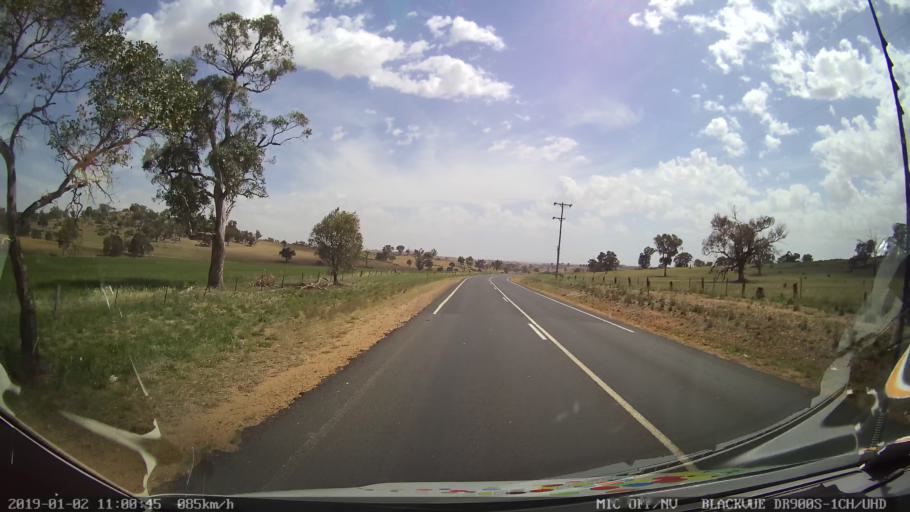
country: AU
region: New South Wales
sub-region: Cootamundra
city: Cootamundra
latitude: -34.6048
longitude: 148.3133
